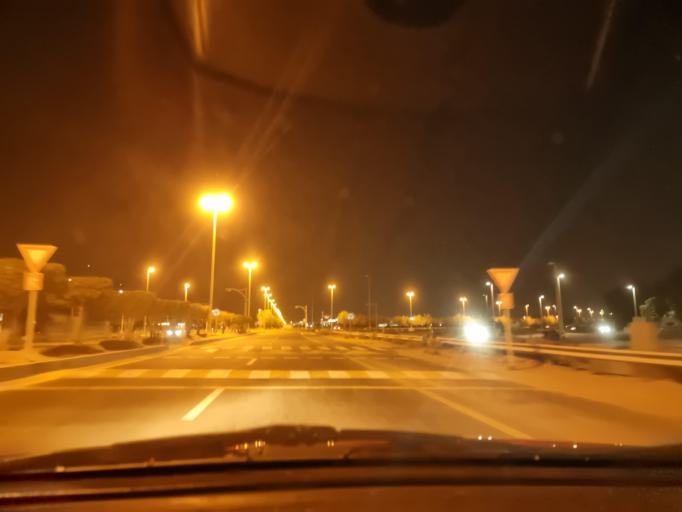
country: AE
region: Abu Dhabi
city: Abu Dhabi
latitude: 24.3737
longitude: 54.6983
